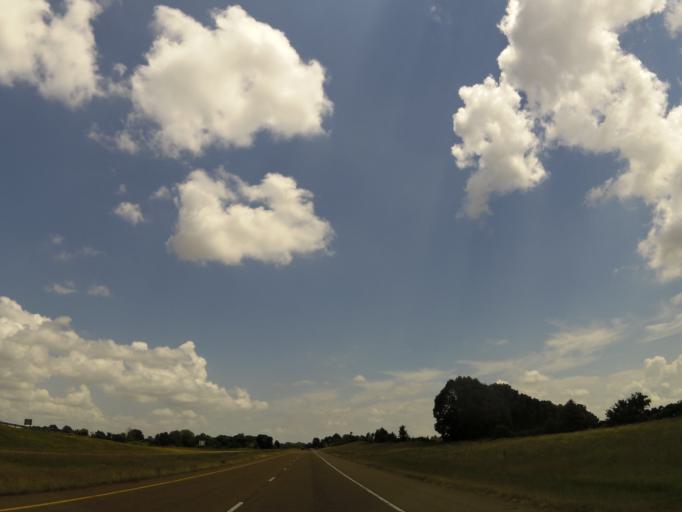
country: US
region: Tennessee
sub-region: Dyer County
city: Dyersburg
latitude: 35.9650
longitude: -89.3306
